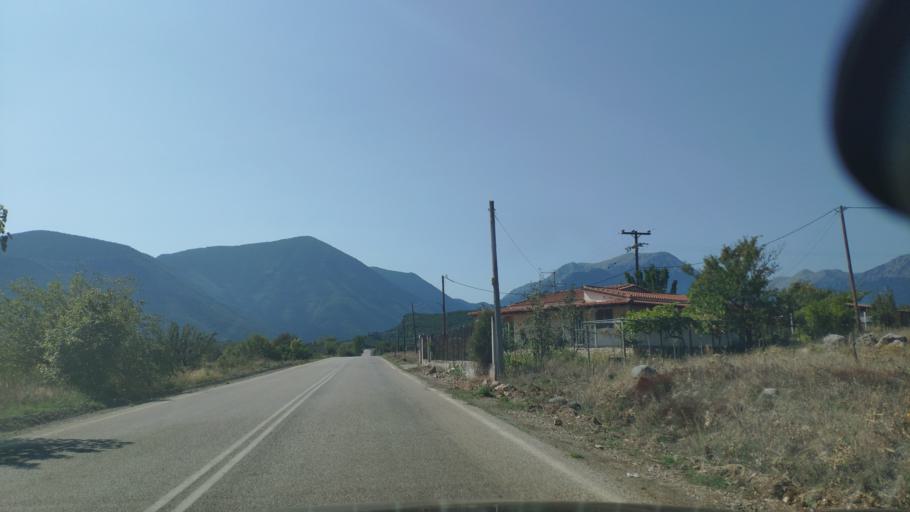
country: GR
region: Peloponnese
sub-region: Nomos Korinthias
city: Nemea
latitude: 37.8660
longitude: 22.4568
